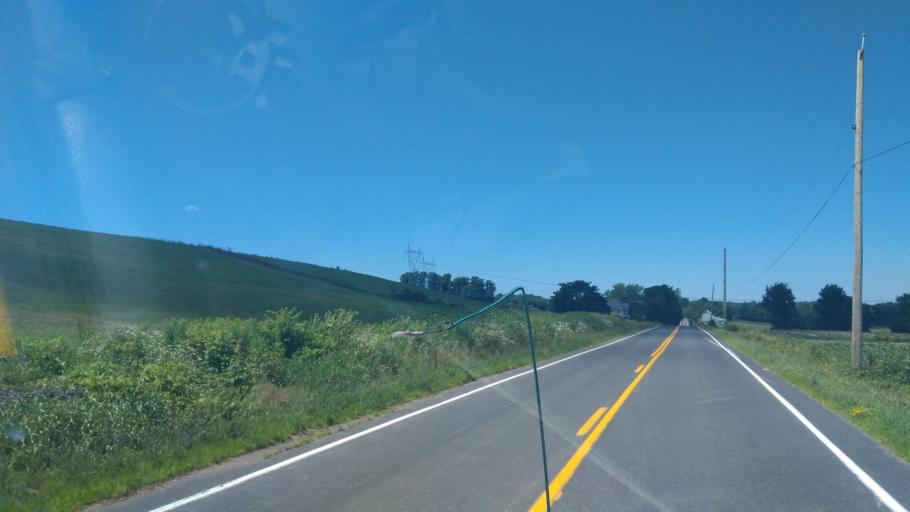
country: US
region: New York
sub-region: Wayne County
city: Lyons
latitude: 43.1271
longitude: -76.9581
